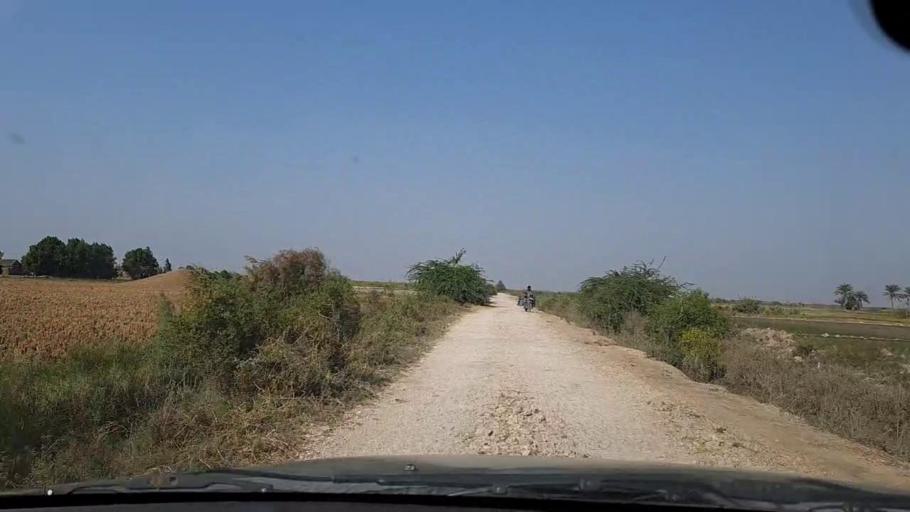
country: PK
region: Sindh
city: Mirpur Sakro
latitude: 24.3744
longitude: 67.6830
